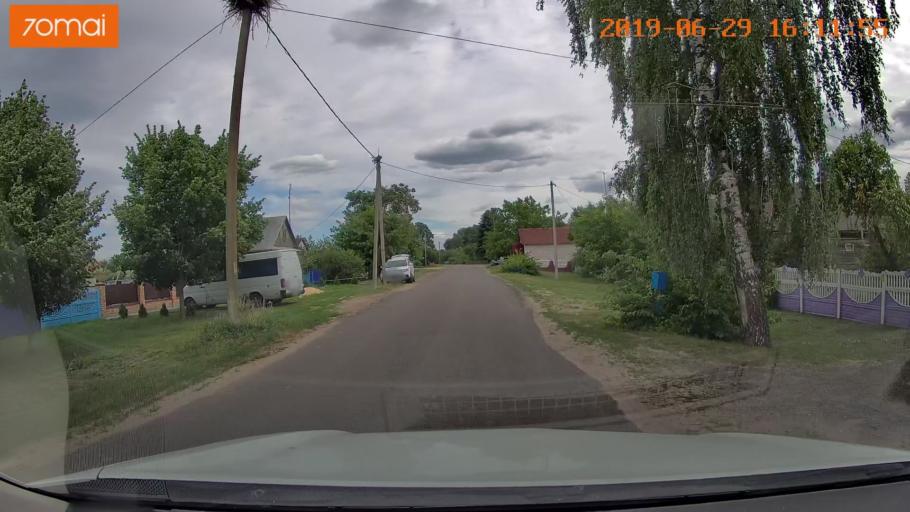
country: BY
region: Brest
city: Luninyets
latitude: 52.2027
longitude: 27.0125
